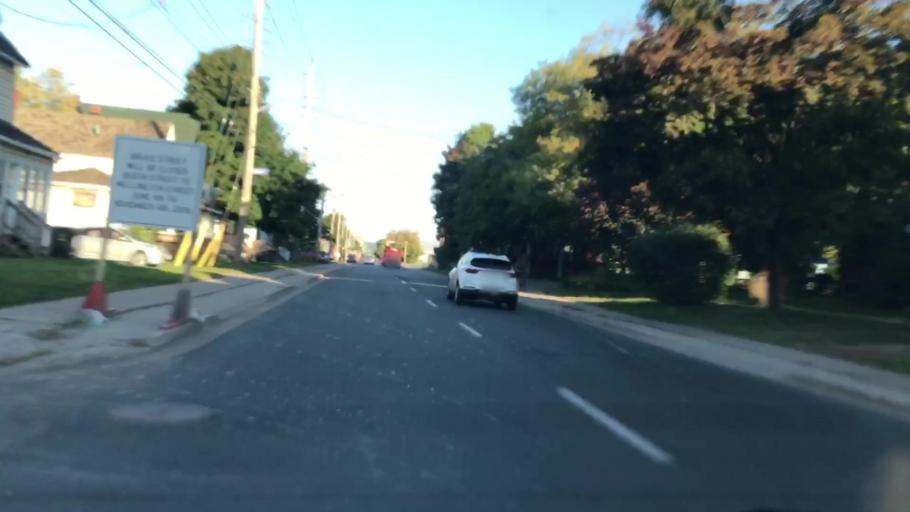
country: CA
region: Ontario
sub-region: Algoma
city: Sault Ste. Marie
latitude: 46.5139
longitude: -84.3312
